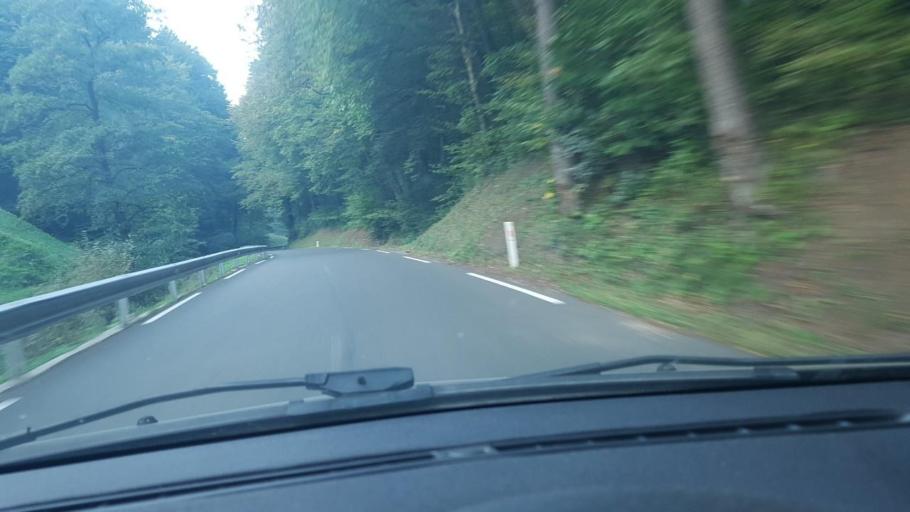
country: SI
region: Rogatec
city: Rogatec
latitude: 46.2734
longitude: 15.7122
